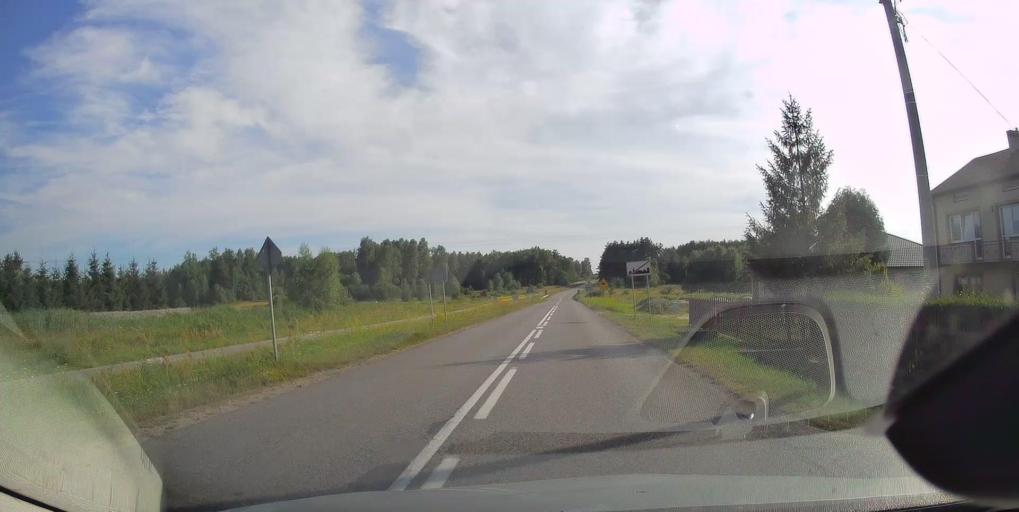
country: PL
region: Swietokrzyskie
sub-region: Powiat konecki
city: Radoszyce
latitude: 51.0820
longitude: 20.2851
